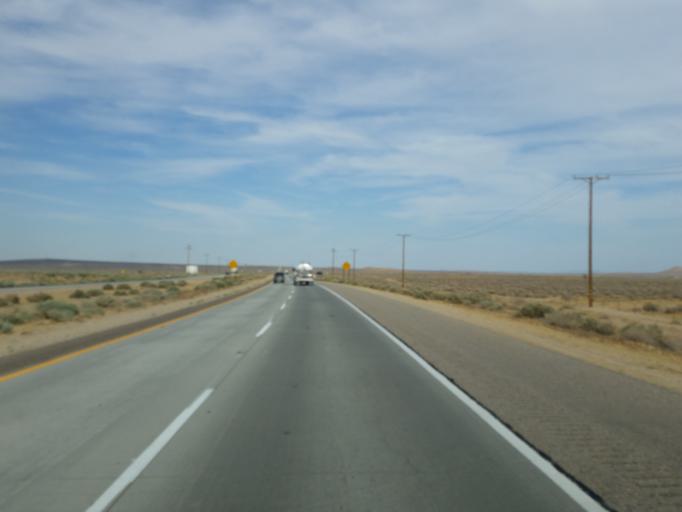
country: US
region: California
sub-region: Kern County
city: Mojave
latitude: 35.0301
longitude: -118.0923
